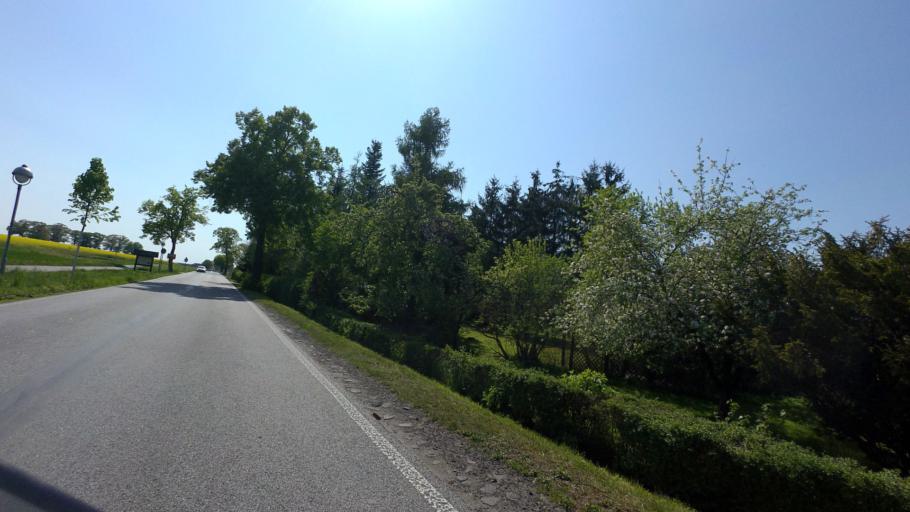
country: DE
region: Brandenburg
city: Tauche
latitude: 52.0833
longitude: 14.1639
